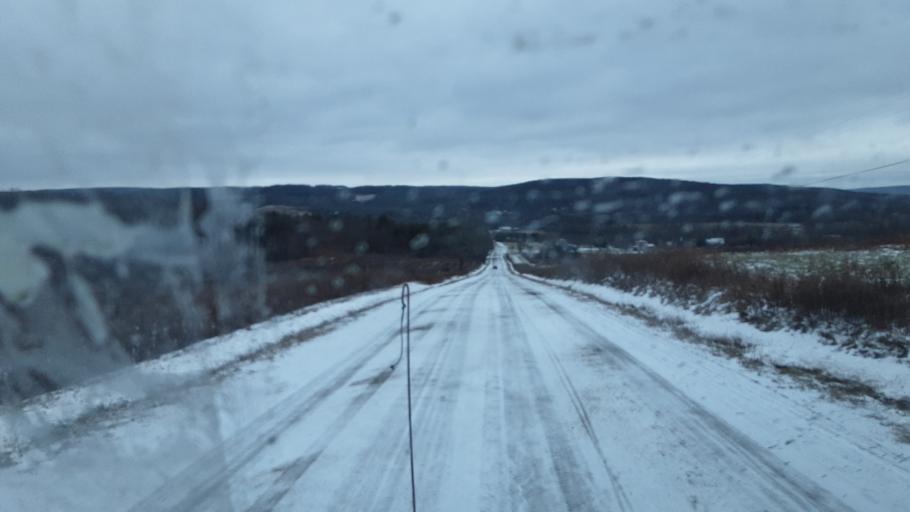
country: US
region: New York
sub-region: Allegany County
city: Friendship
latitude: 42.2874
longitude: -78.1624
